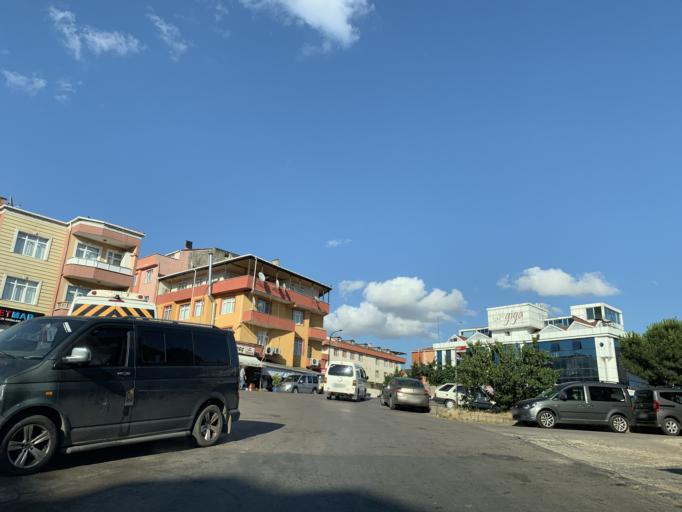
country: TR
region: Istanbul
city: Pendik
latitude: 40.8955
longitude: 29.2520
